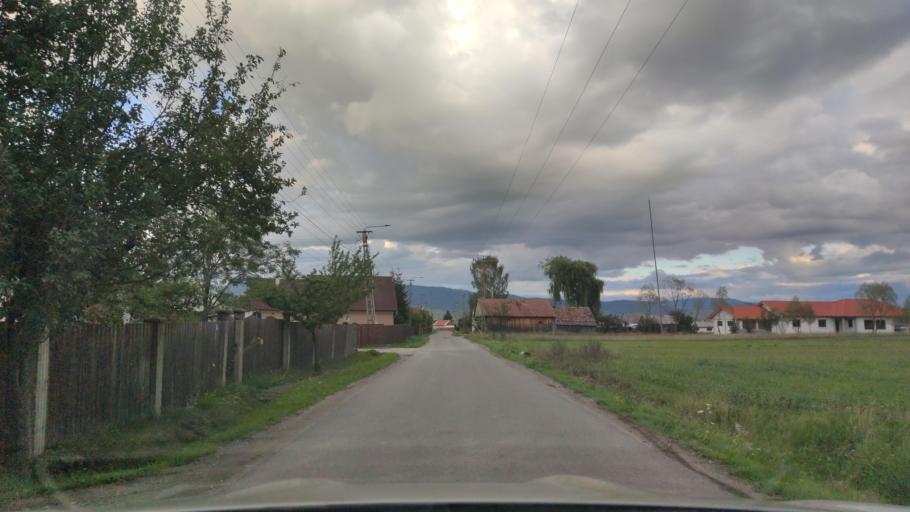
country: RO
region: Harghita
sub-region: Comuna Remetea
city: Remetea
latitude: 46.8050
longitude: 25.4453
